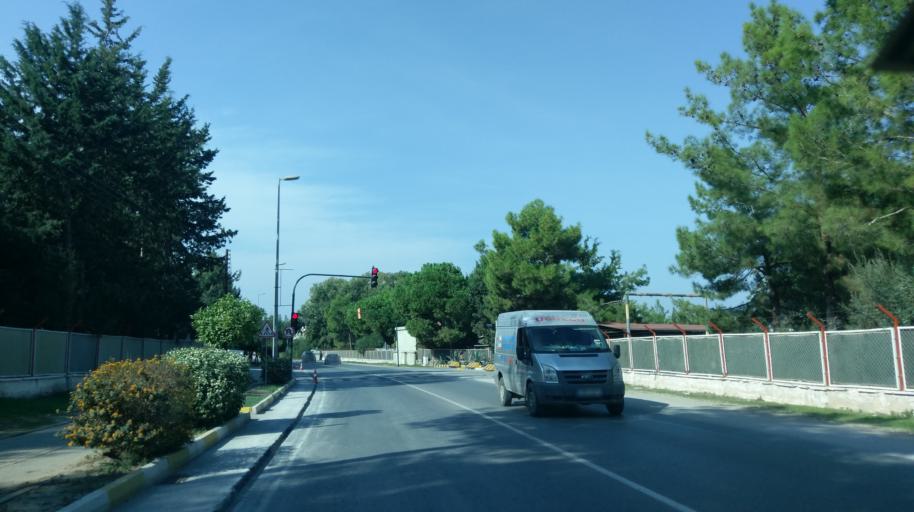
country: CY
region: Keryneia
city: Kyrenia
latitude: 35.3395
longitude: 33.2982
